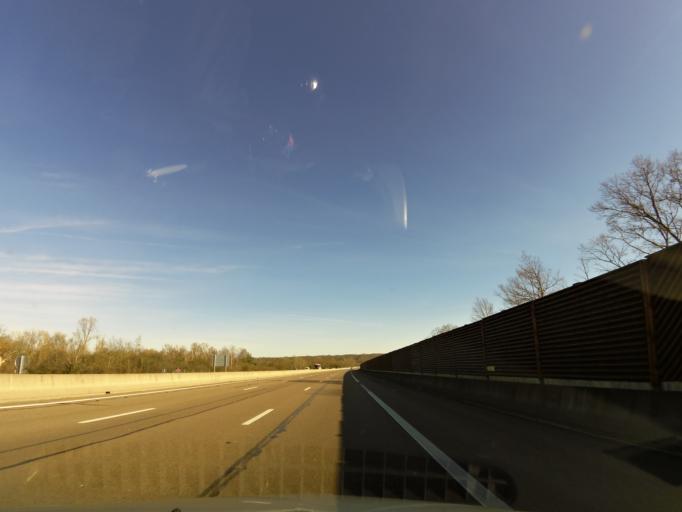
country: FR
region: Bourgogne
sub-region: Departement de l'Yonne
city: Gurgy
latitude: 47.8558
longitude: 3.5610
